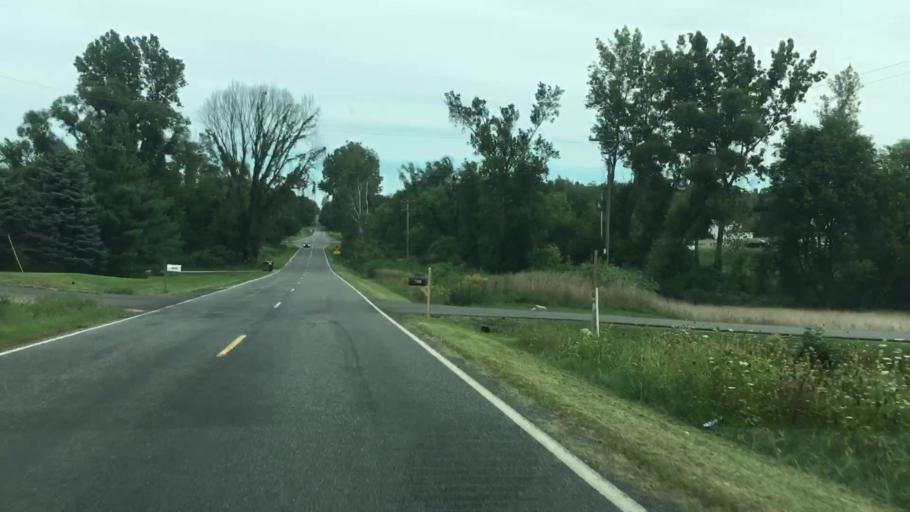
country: US
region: Michigan
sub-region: Kent County
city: Byron Center
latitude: 42.8236
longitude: -85.7828
